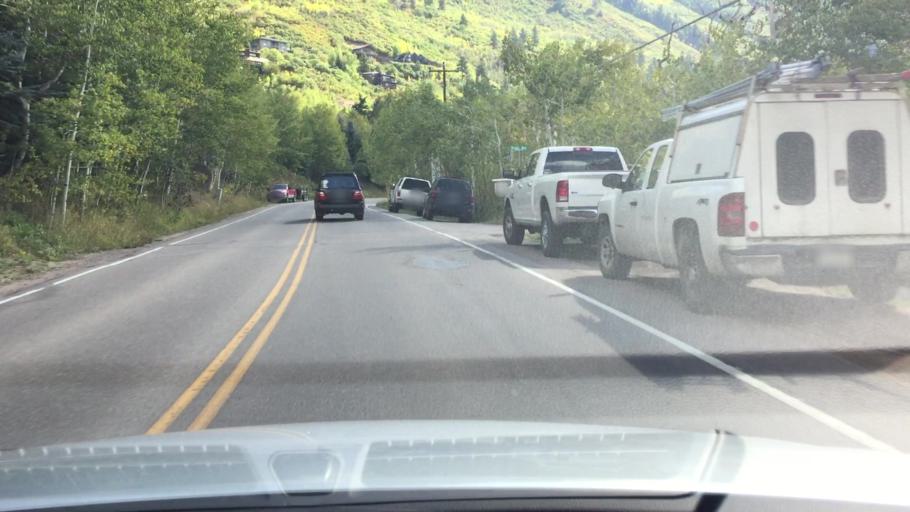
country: US
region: Colorado
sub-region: Pitkin County
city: Aspen
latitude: 39.1819
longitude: -106.8048
